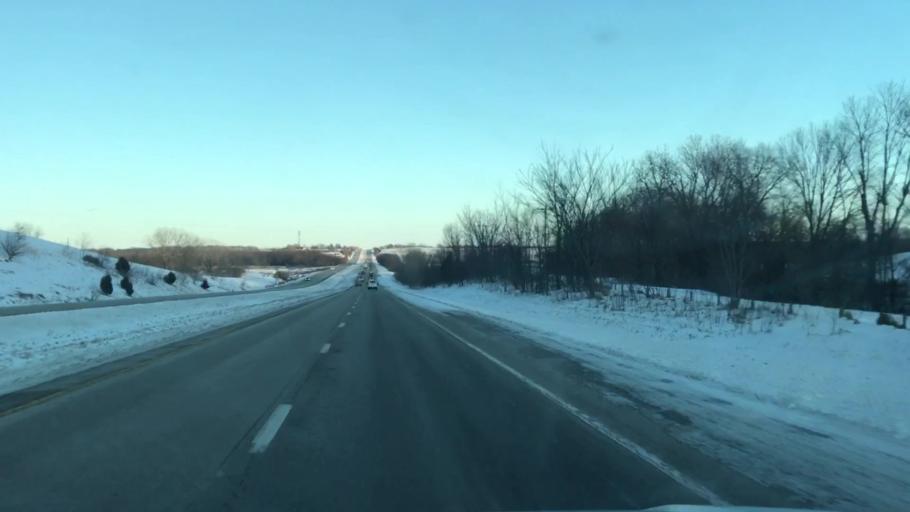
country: US
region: Missouri
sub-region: Clinton County
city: Gower
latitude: 39.7474
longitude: -94.6753
